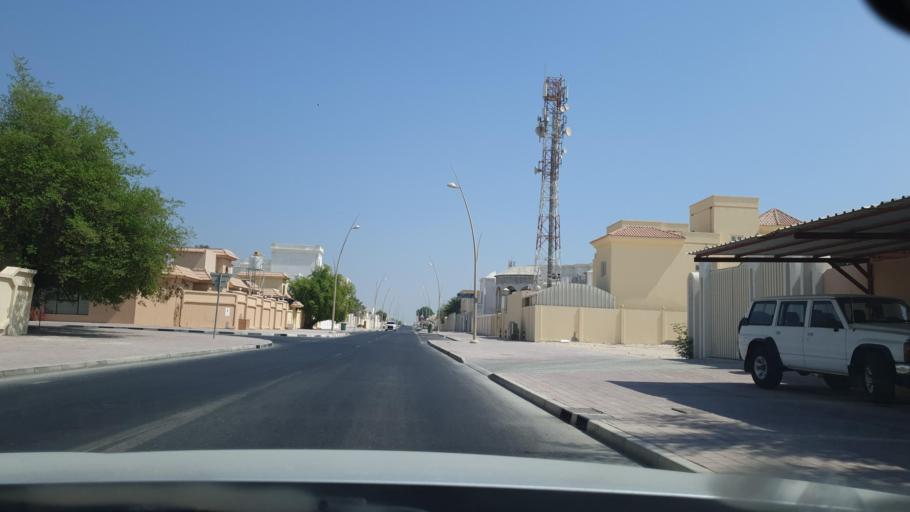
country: QA
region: Al Khawr
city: Al Khawr
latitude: 25.6827
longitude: 51.5178
